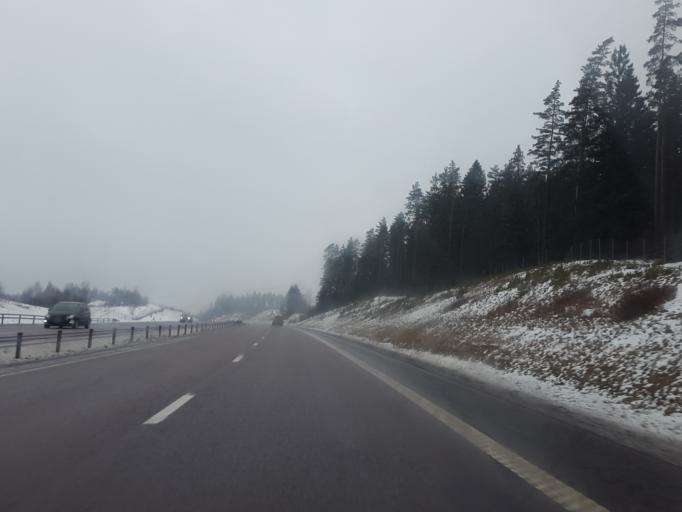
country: SE
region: Vaestra Goetaland
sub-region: Boras Kommun
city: Dalsjofors
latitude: 57.7827
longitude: 13.1211
